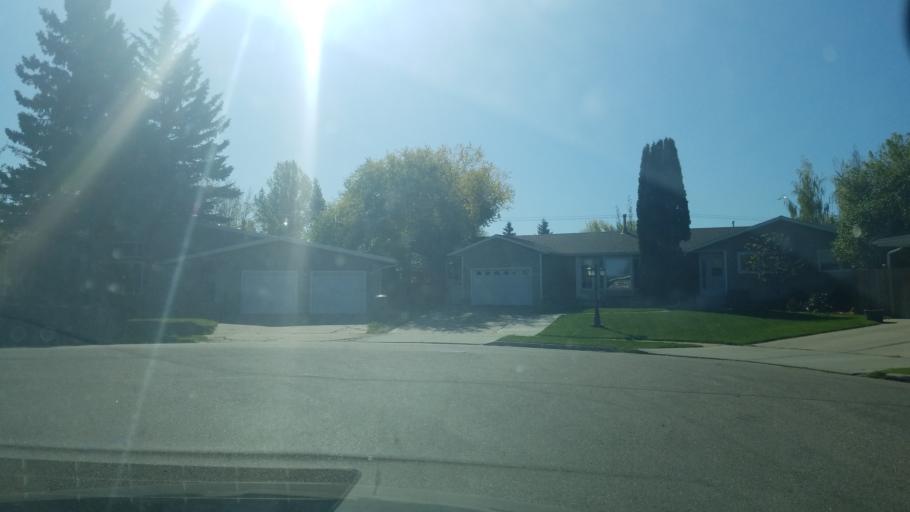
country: CA
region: Saskatchewan
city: Lloydminster
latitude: 53.2715
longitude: -110.0203
